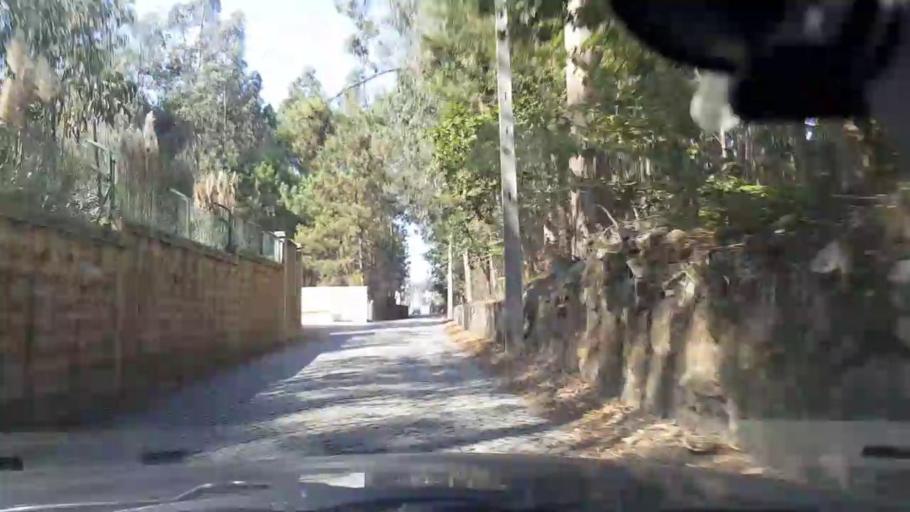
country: PT
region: Porto
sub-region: Povoa de Varzim
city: Pedroso
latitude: 41.3927
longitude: -8.7135
